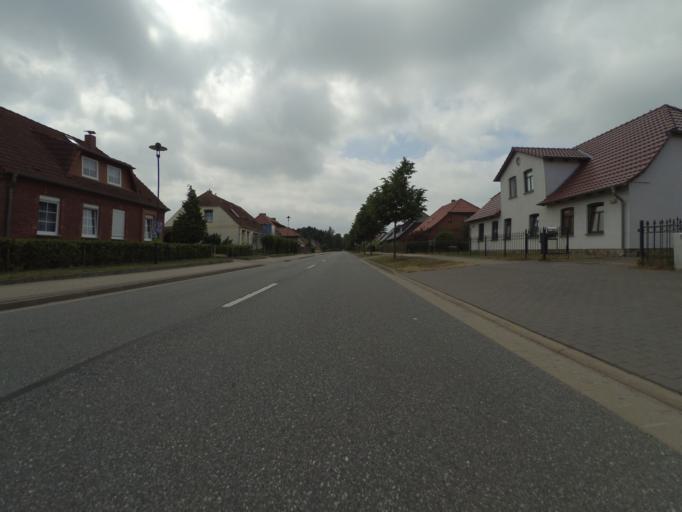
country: DE
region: Mecklenburg-Vorpommern
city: Malchow
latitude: 53.5320
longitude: 12.4239
